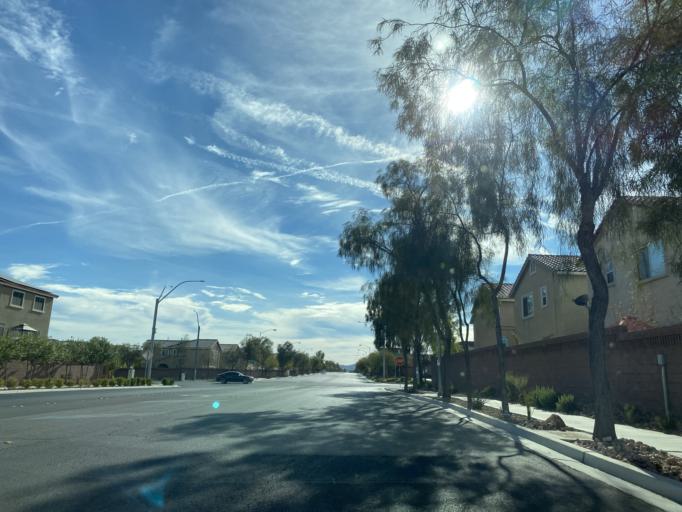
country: US
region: Nevada
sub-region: Clark County
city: Enterprise
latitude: 36.0569
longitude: -115.2340
